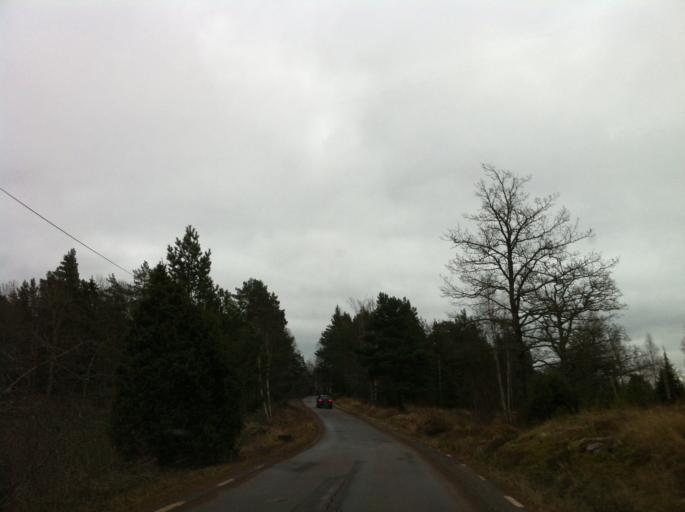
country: SE
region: Kalmar
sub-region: Vasterviks Kommun
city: Forserum
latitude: 57.9260
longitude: 16.5446
